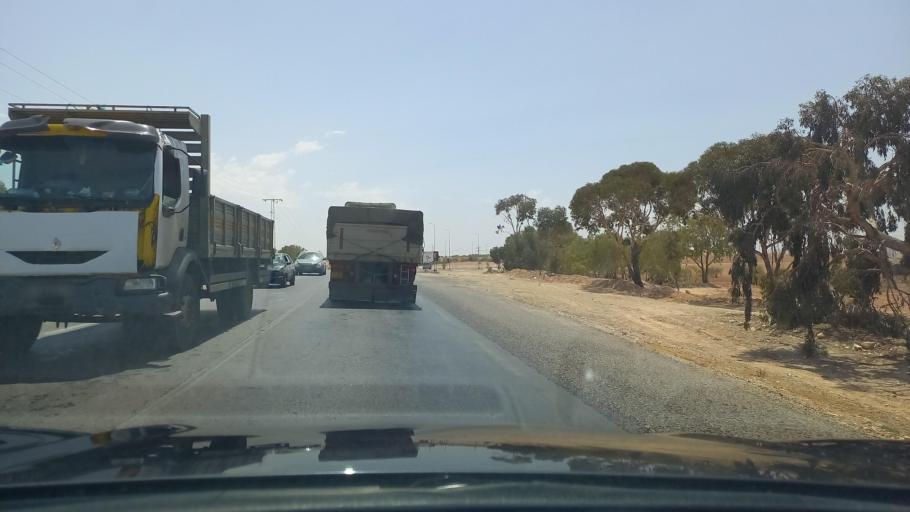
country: TN
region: Madanin
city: Medenine
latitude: 33.5678
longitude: 10.3171
